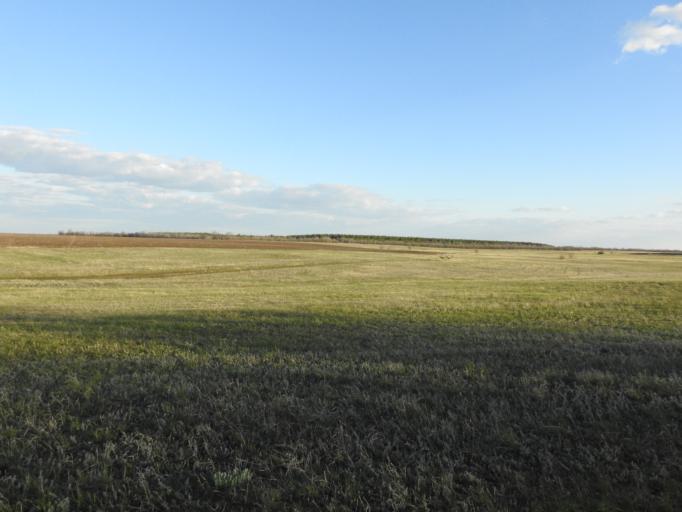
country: RU
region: Saratov
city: Krasnyy Yar
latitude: 51.5798
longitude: 46.5848
